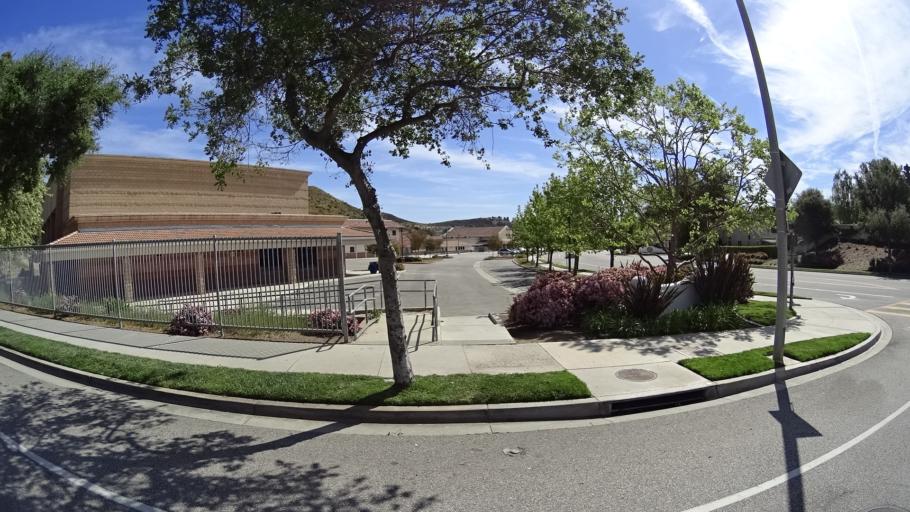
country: US
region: California
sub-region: Ventura County
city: Casa Conejo
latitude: 34.1730
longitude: -118.9754
